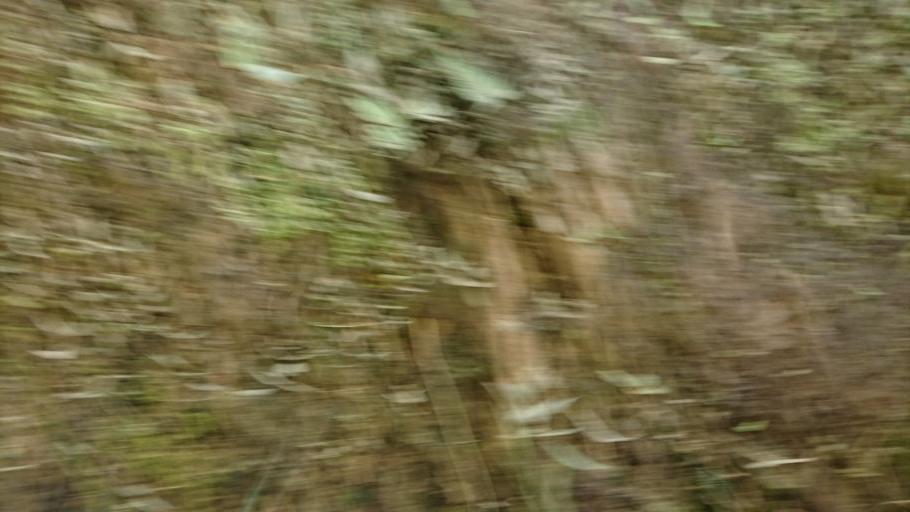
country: BO
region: La Paz
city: Coroico
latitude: -16.1306
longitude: -67.7631
